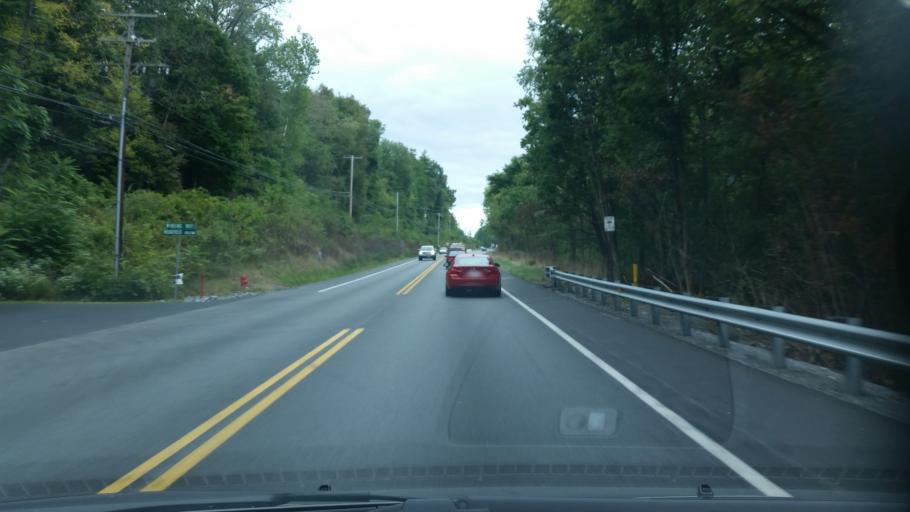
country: US
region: Pennsylvania
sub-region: Lancaster County
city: Willow Street
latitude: 40.0014
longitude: -76.2922
